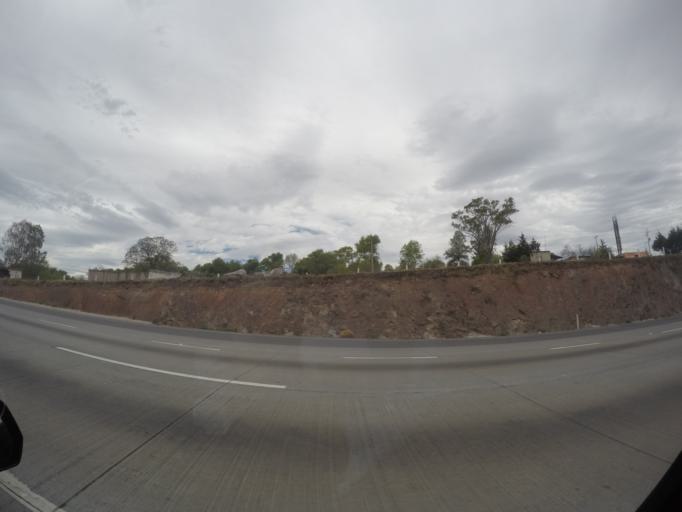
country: MX
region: Hidalgo
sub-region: Tepeji del Rio de Ocampo
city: Santiago Tlautla
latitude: 19.9778
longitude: -99.4362
